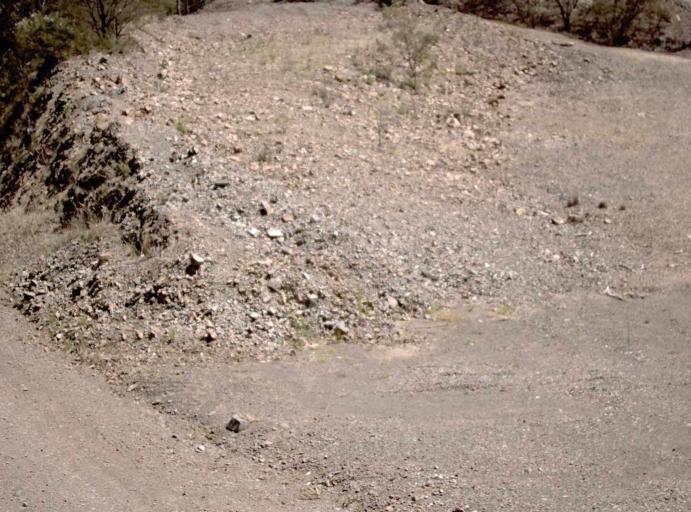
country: AU
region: New South Wales
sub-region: Bombala
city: Bombala
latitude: -37.1019
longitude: 148.6362
